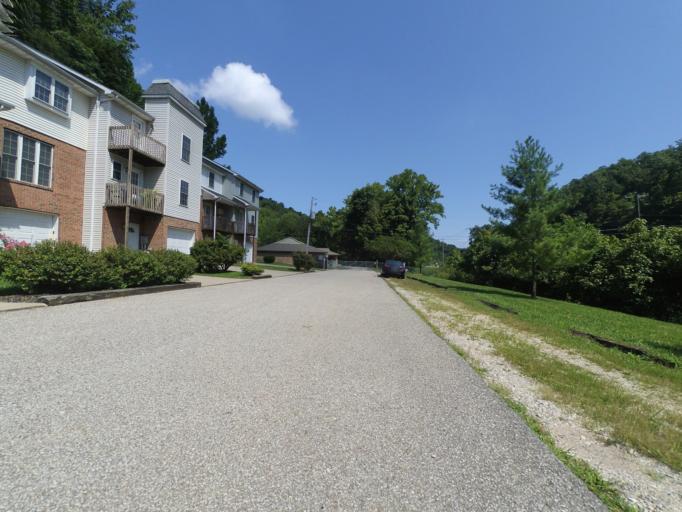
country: US
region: West Virginia
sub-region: Cabell County
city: Huntington
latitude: 38.3841
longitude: -82.4576
